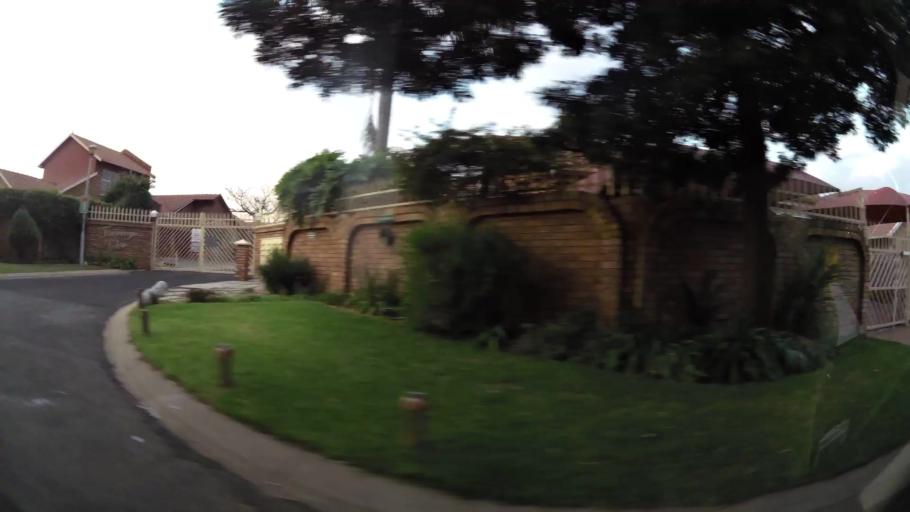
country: ZA
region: Gauteng
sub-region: Ekurhuleni Metropolitan Municipality
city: Benoni
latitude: -26.1687
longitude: 28.3073
